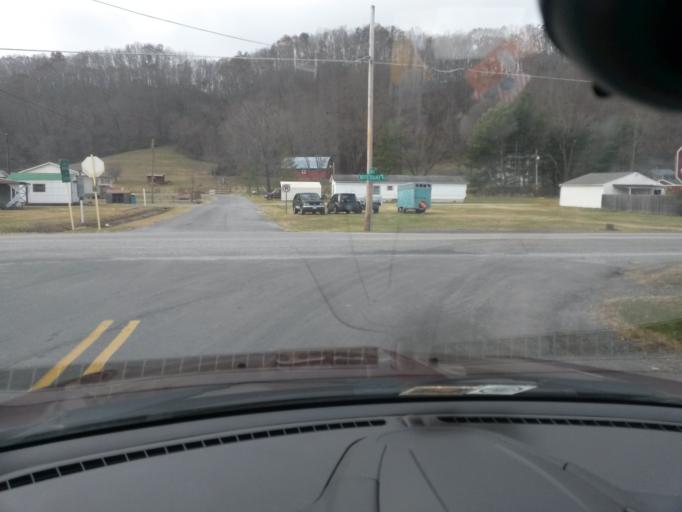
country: US
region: Virginia
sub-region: Alleghany County
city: Clifton Forge
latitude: 37.7932
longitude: -79.7867
